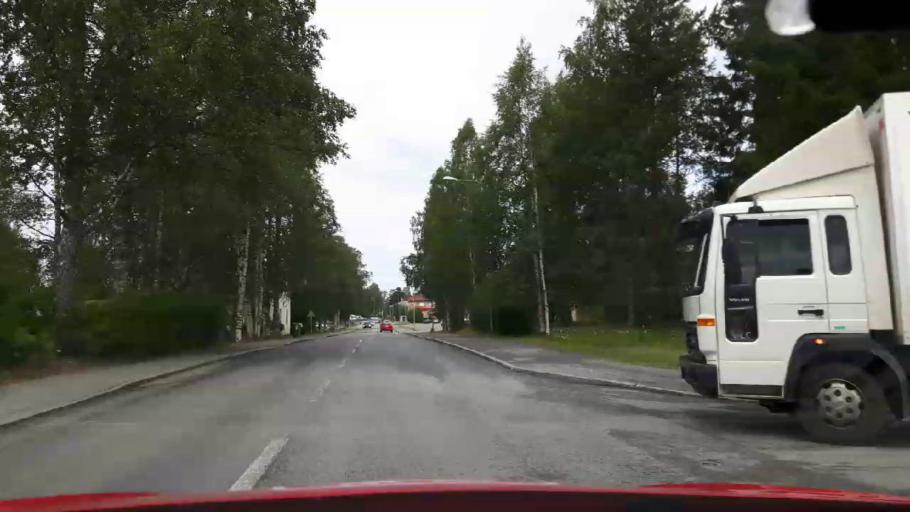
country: SE
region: Jaemtland
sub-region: Stroemsunds Kommun
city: Stroemsund
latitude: 63.8495
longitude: 15.5620
